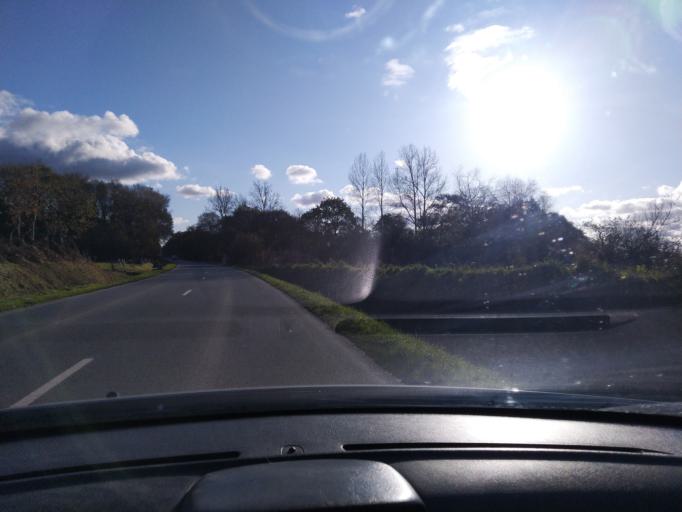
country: FR
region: Brittany
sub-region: Departement des Cotes-d'Armor
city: Plestin-les-Greves
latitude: 48.6195
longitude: -3.6197
